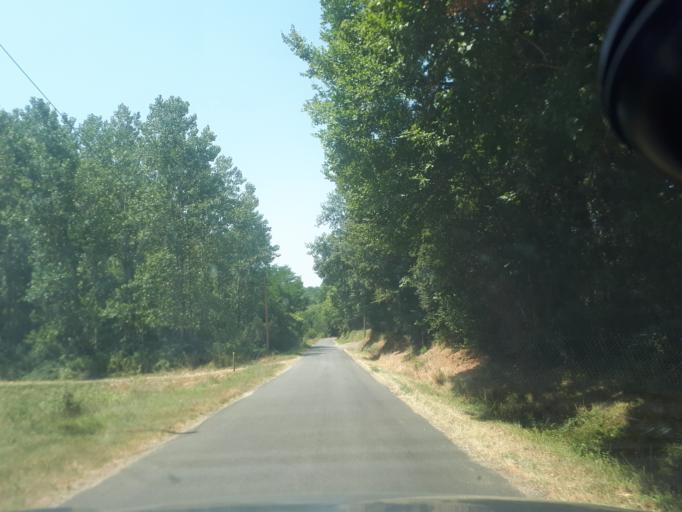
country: FR
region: Midi-Pyrenees
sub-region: Departement du Lot
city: Salviac
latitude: 44.7369
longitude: 1.2792
